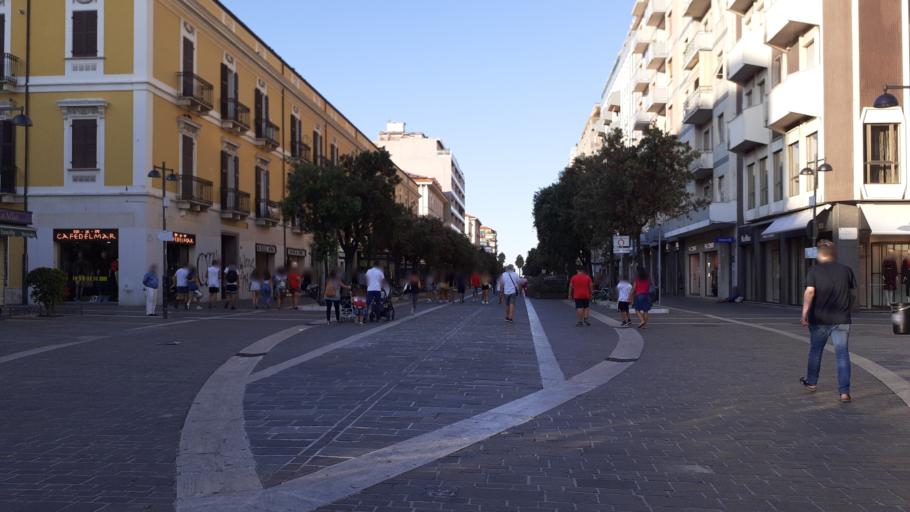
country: IT
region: Abruzzo
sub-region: Provincia di Pescara
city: Pescara
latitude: 42.4704
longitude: 14.2067
